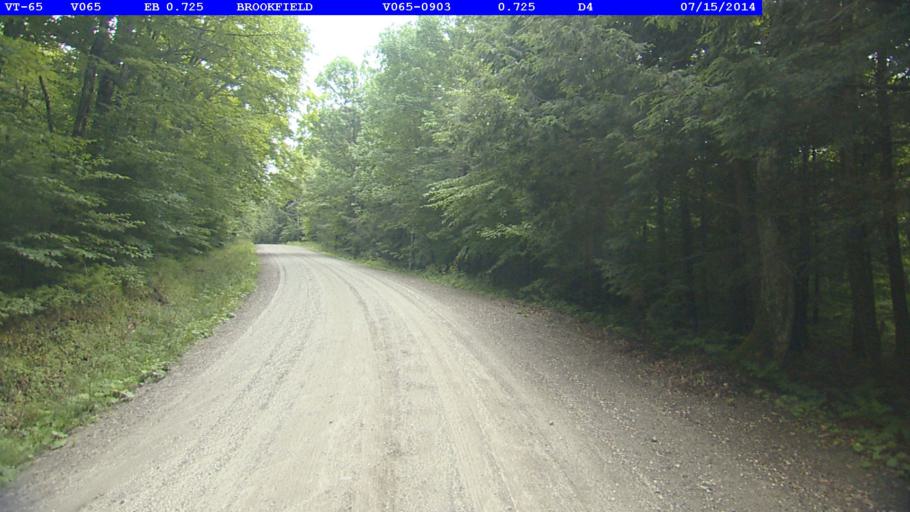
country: US
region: Vermont
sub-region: Washington County
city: Northfield
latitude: 44.0587
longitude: -72.6300
